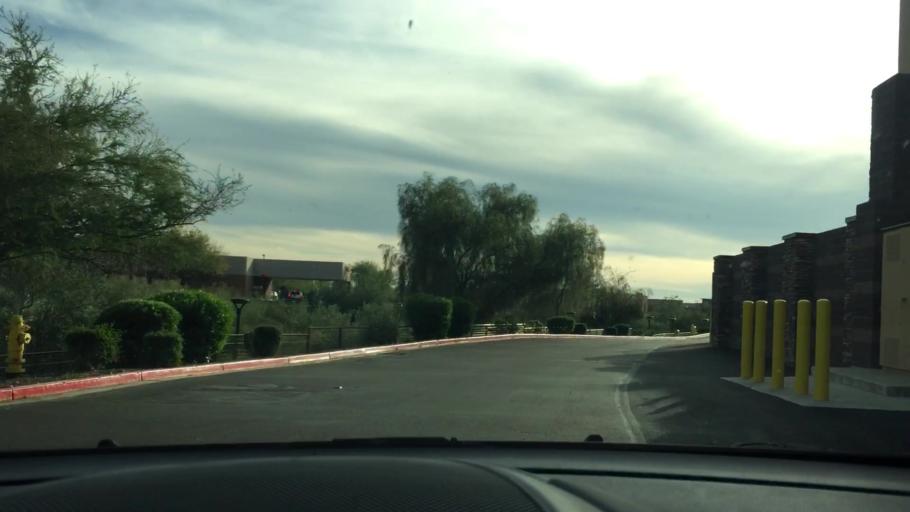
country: US
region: Arizona
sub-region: Maricopa County
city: Sun City West
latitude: 33.7144
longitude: -112.2730
